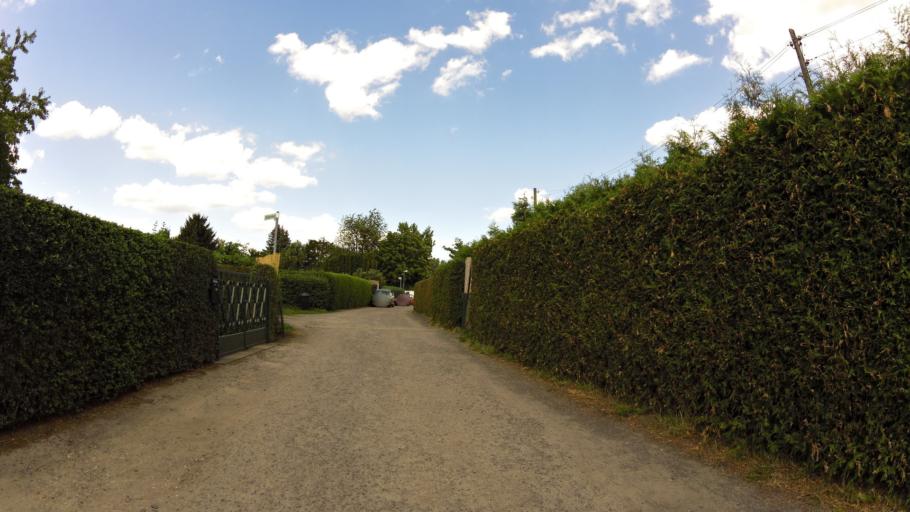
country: DE
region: Berlin
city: Rosenthal
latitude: 52.5975
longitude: 13.3908
